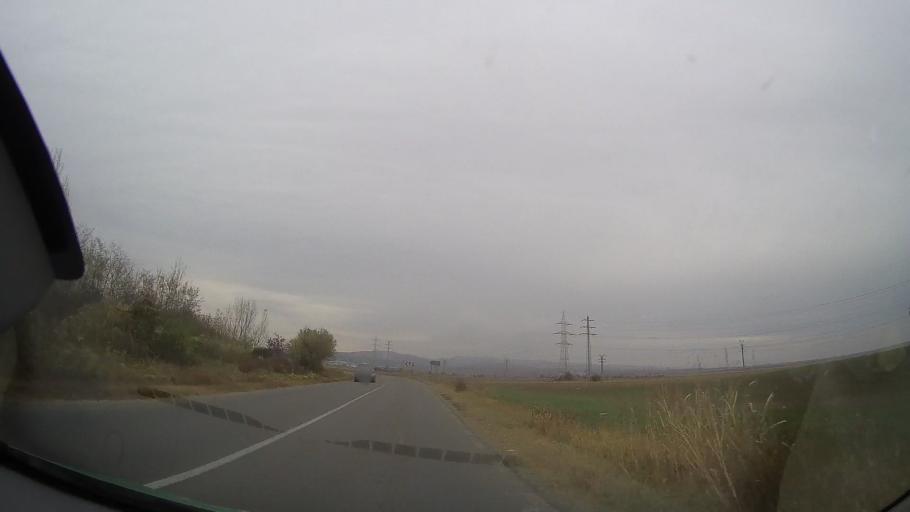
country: RO
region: Prahova
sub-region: Oras Urlati
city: Urlati
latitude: 44.9644
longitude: 26.2343
